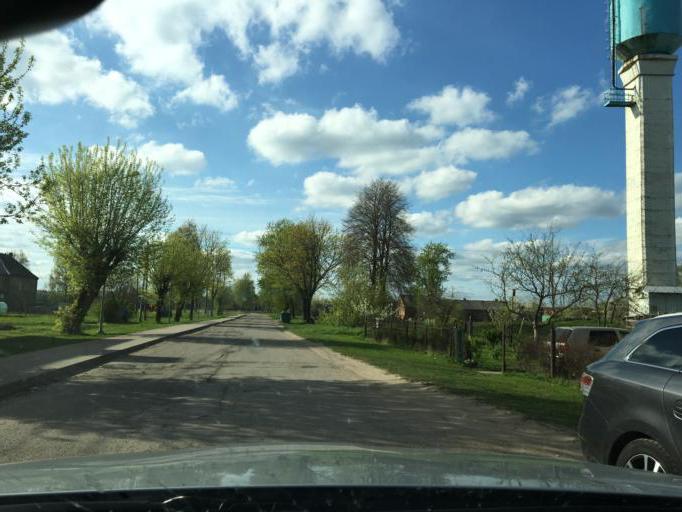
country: LV
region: Ozolnieku
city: Ozolnieki
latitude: 56.6826
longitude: 23.8482
